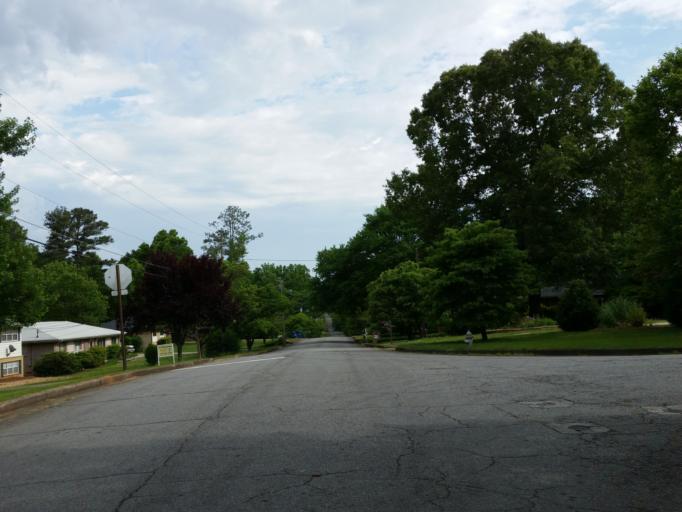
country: US
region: Georgia
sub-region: Cherokee County
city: Woodstock
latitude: 34.0299
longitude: -84.4837
